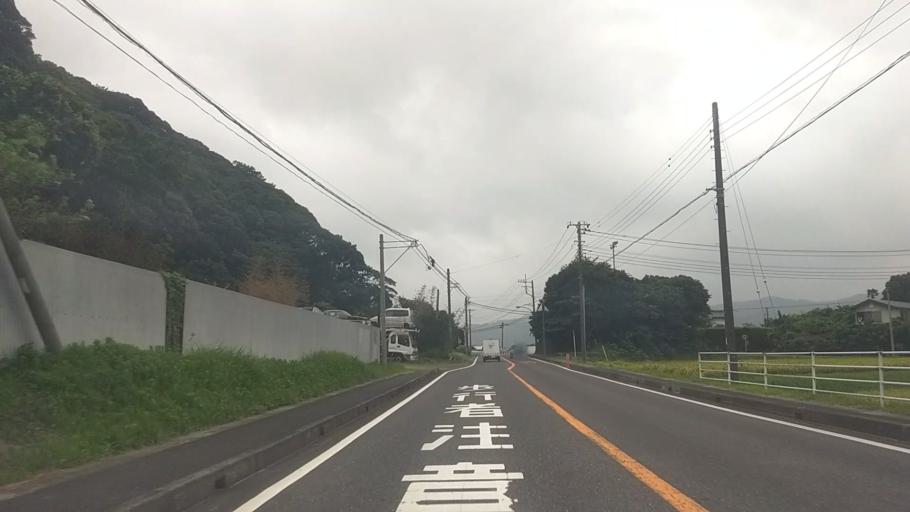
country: JP
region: Chiba
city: Kawaguchi
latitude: 35.1306
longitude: 140.0790
